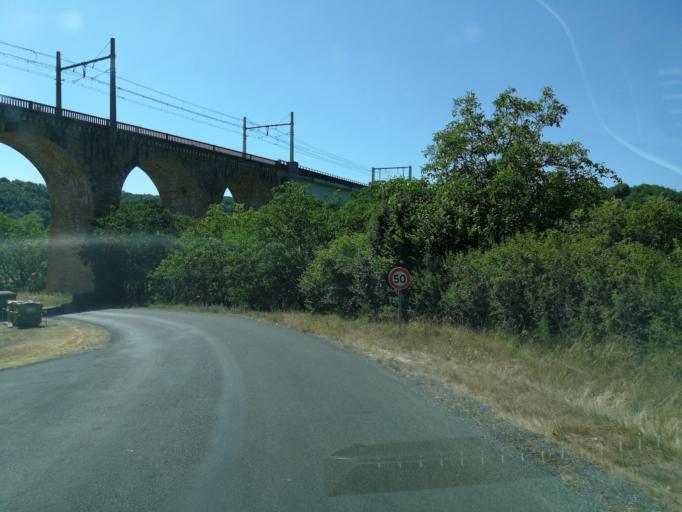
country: FR
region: Midi-Pyrenees
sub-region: Departement du Lot
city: Souillac
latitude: 44.9089
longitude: 1.4784
